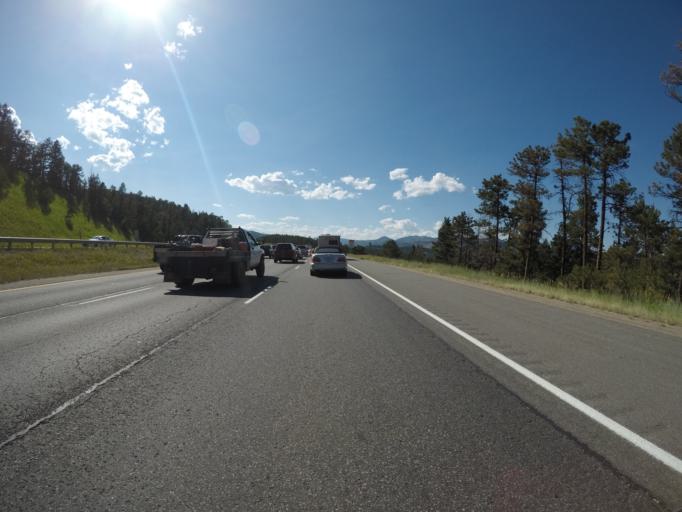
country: US
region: Colorado
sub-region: Jefferson County
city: Kittredge
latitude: 39.7097
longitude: -105.3489
